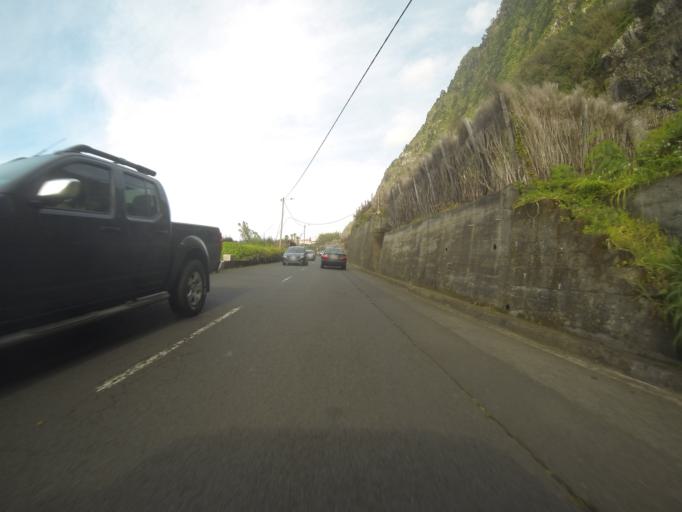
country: PT
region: Madeira
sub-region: Sao Vicente
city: Sao Vicente
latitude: 32.8112
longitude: -17.0393
